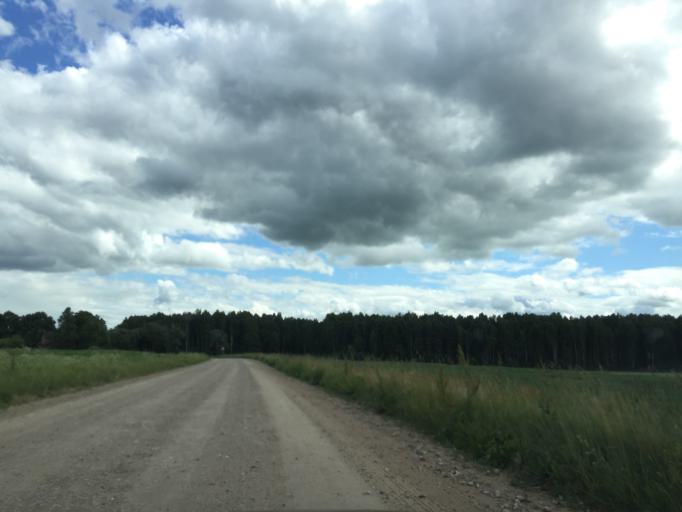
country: LV
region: Vecumnieki
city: Vecumnieki
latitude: 56.4684
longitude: 24.4244
